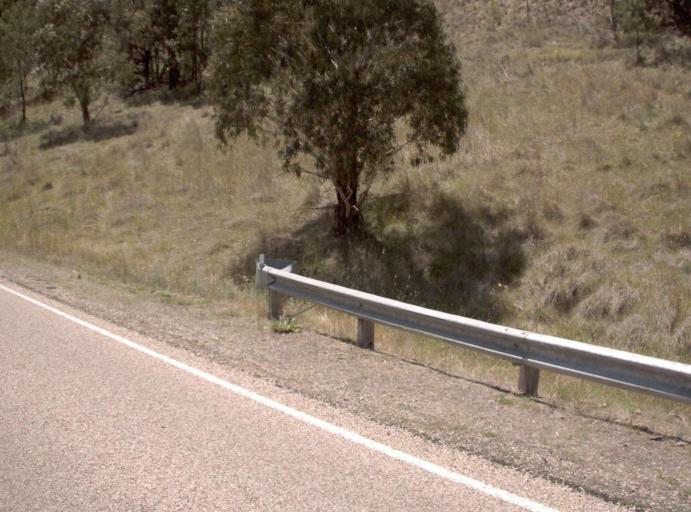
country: AU
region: Victoria
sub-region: Alpine
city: Mount Beauty
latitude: -37.1641
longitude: 147.6632
